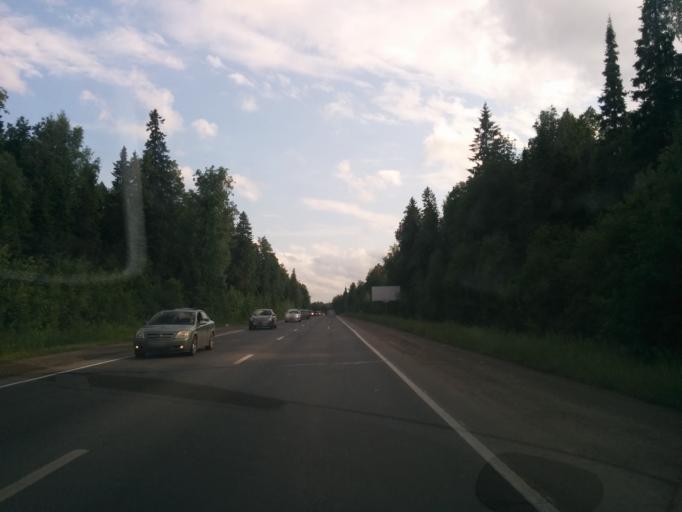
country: RU
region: Perm
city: Polazna
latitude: 58.1064
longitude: 56.4256
